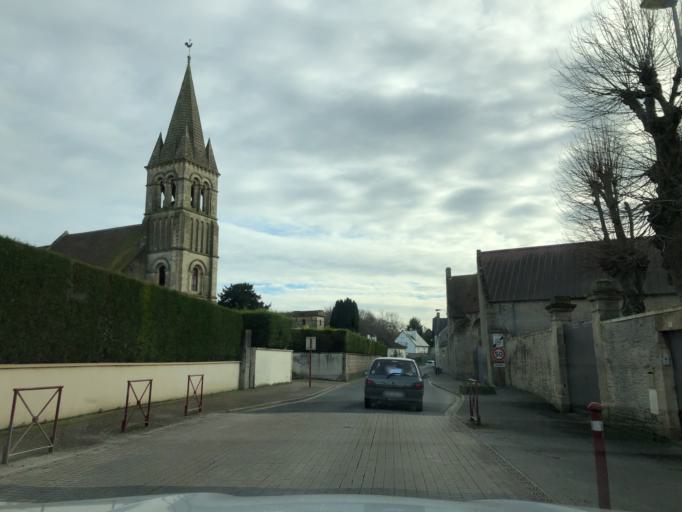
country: FR
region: Lower Normandy
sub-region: Departement du Calvados
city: Beuville
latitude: 49.2432
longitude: -0.3284
